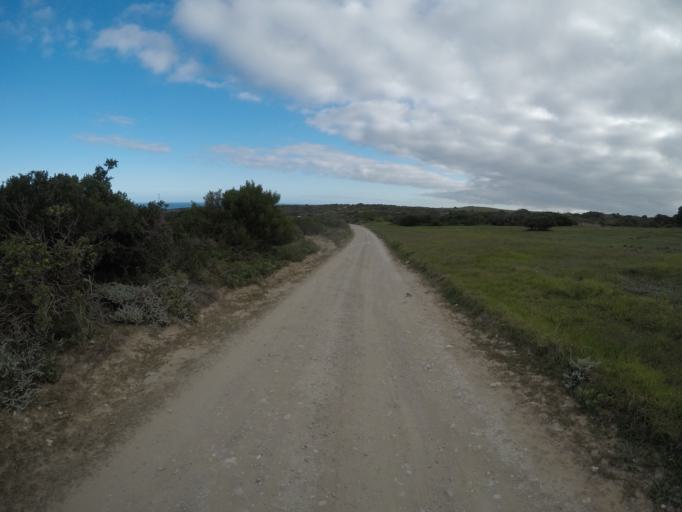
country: ZA
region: Western Cape
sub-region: Eden District Municipality
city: Riversdale
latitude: -34.4214
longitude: 21.3316
